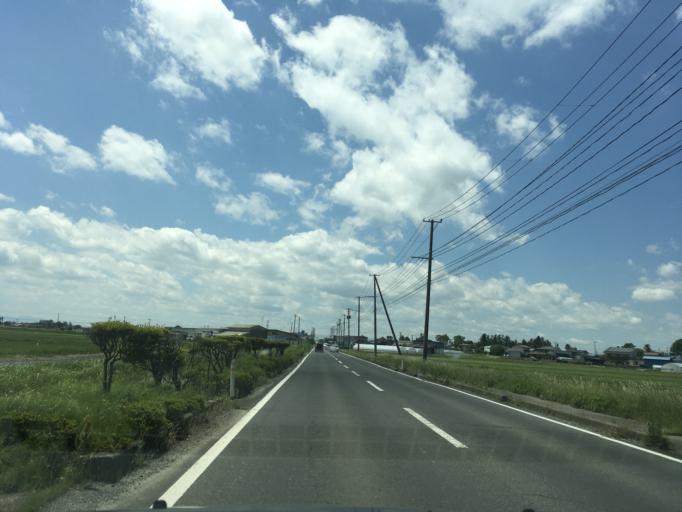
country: JP
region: Miyagi
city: Wakuya
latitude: 38.6787
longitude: 141.2218
